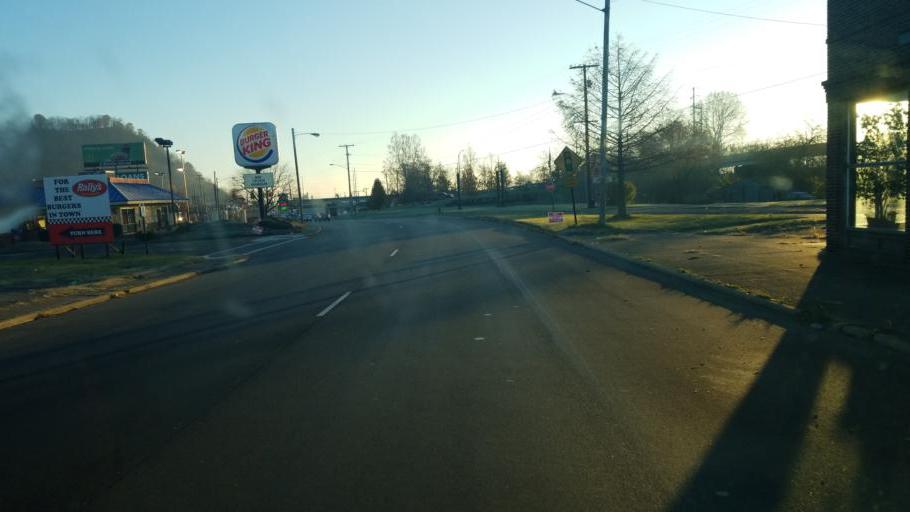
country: US
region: Kentucky
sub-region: Greenup County
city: South Shore
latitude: 38.7386
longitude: -82.9730
